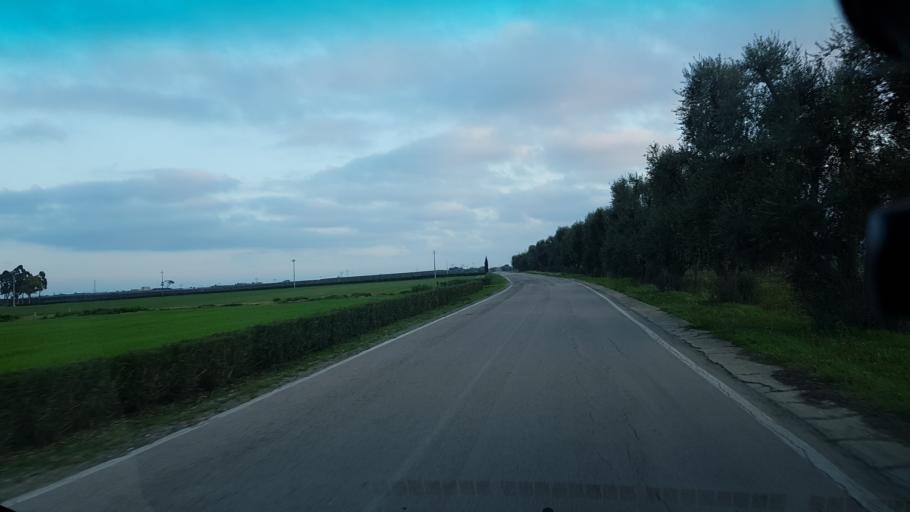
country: IT
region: Apulia
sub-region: Provincia di Brindisi
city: Mesagne
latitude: 40.6040
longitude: 17.7918
